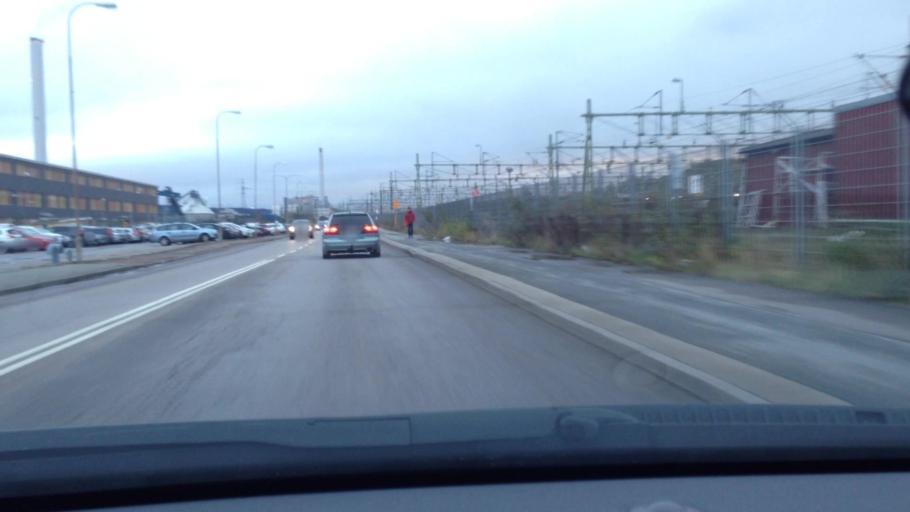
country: SE
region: Vaestra Goetaland
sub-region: Goteborg
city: Eriksbo
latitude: 57.7270
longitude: 12.0275
